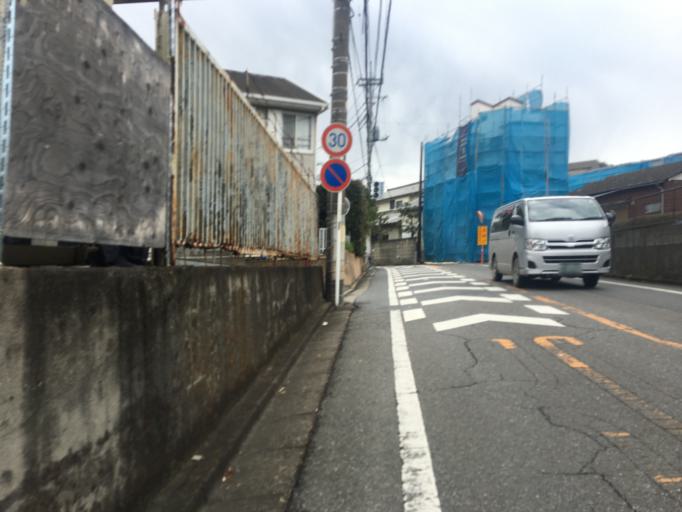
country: JP
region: Saitama
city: Shiki
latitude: 35.8306
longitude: 139.5689
